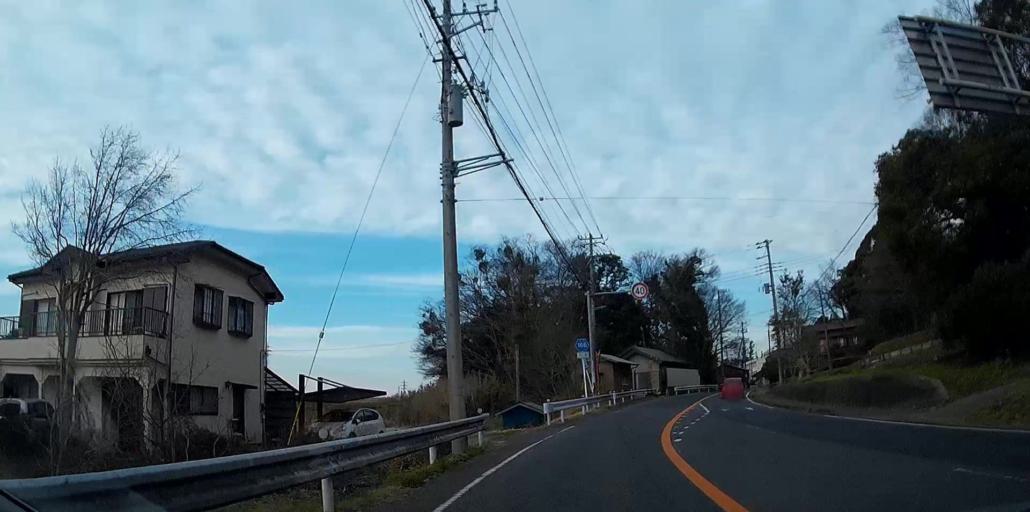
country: JP
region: Chiba
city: Kisarazu
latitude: 35.3566
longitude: 140.0561
